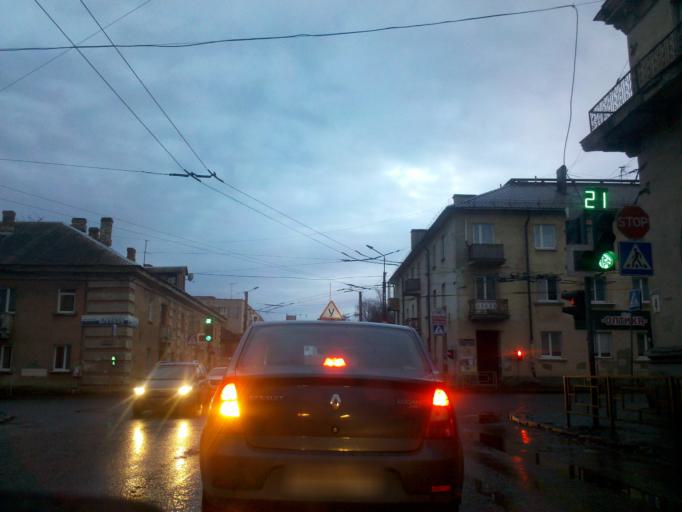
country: RU
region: Republic of Karelia
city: Petrozavodsk
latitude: 61.7841
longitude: 34.3921
